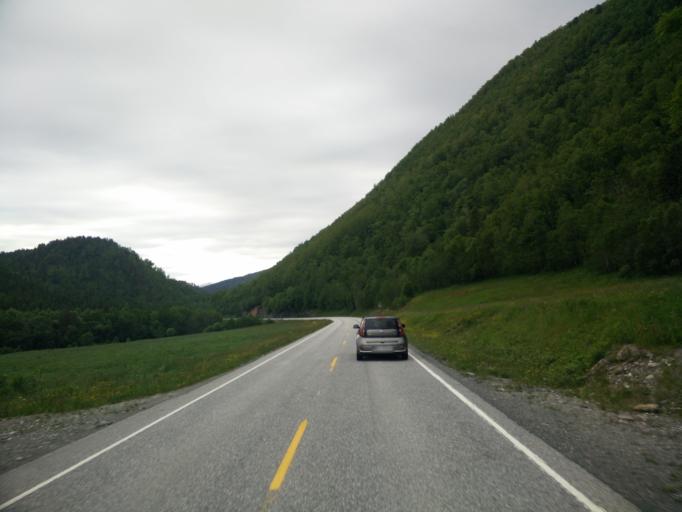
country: NO
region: Sor-Trondelag
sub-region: Hemne
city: Kyrksaeterora
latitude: 63.2096
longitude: 9.1588
